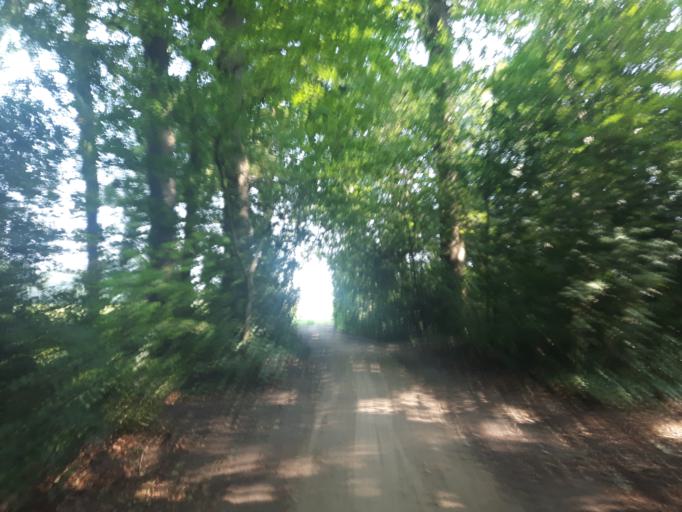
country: NL
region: Overijssel
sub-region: Gemeente Haaksbergen
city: Haaksbergen
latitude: 52.2046
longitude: 6.7380
